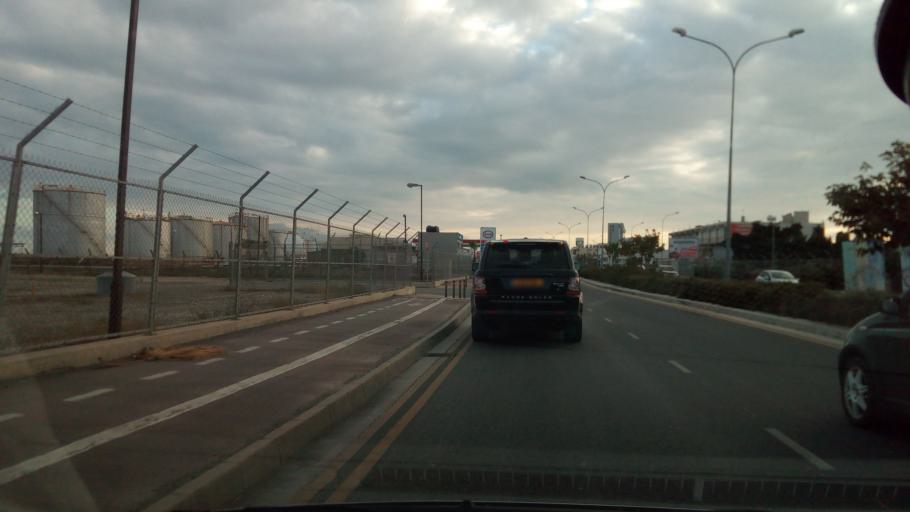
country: CY
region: Larnaka
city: Livadia
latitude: 34.9399
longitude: 33.6419
